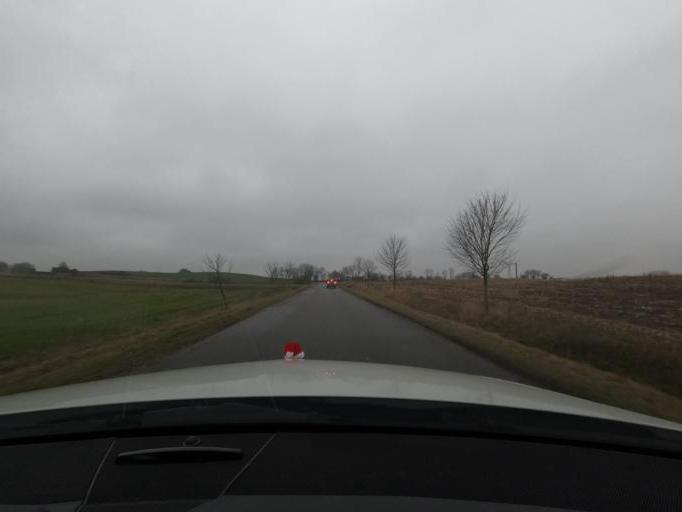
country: DK
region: South Denmark
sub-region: Haderslev Kommune
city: Haderslev
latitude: 55.1949
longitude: 9.4729
